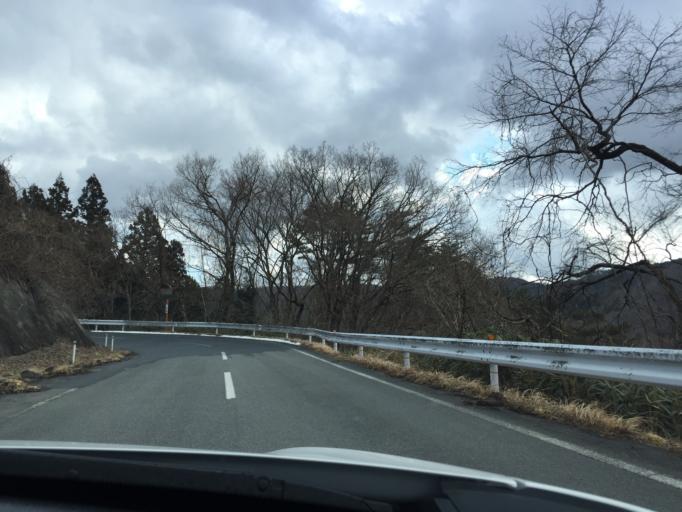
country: JP
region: Fukushima
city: Iwaki
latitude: 37.2114
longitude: 140.7468
